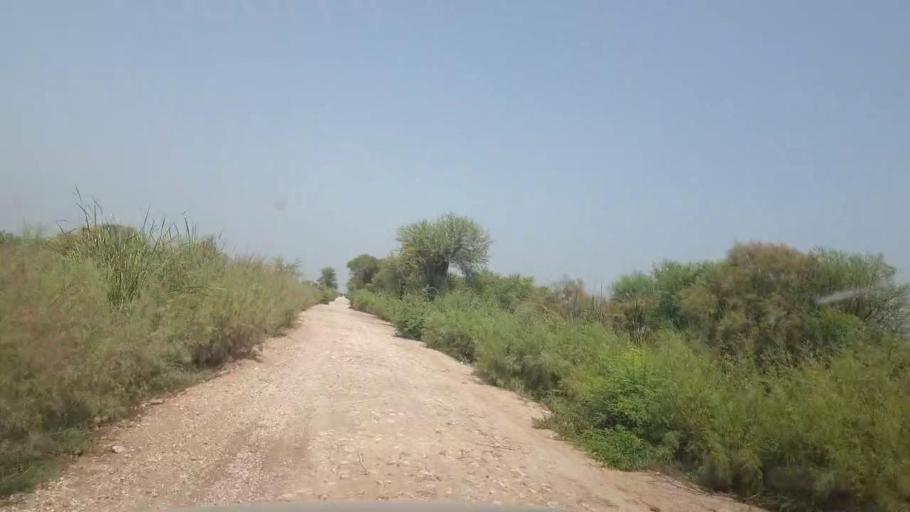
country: PK
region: Sindh
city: Lakhi
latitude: 27.8358
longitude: 68.6247
